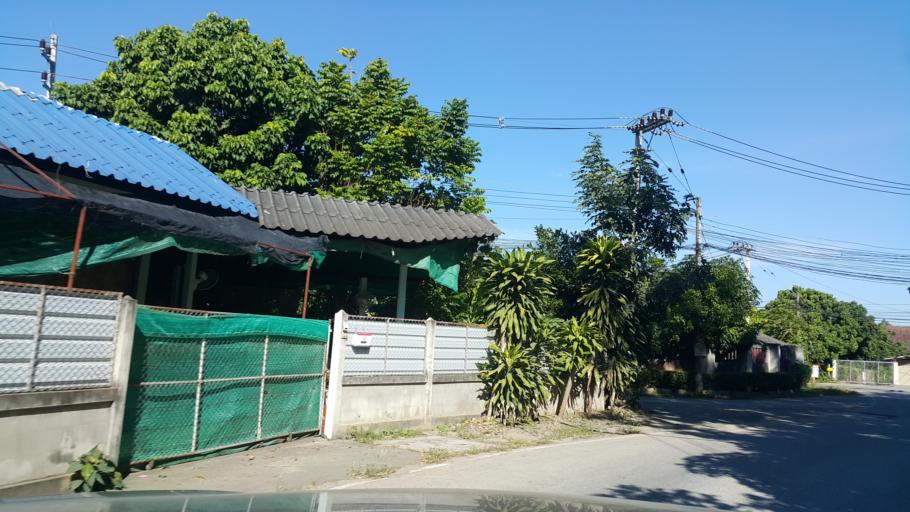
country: TH
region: Chiang Mai
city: San Sai
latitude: 18.8489
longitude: 98.9917
